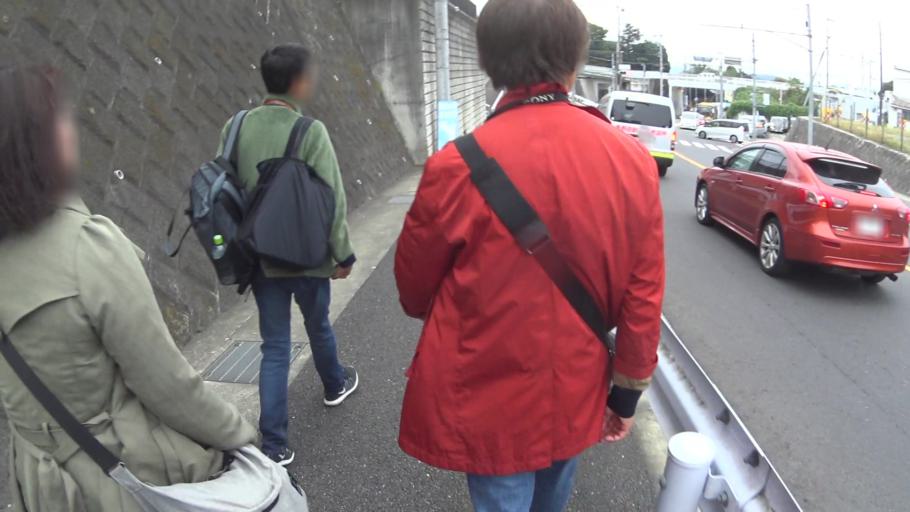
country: JP
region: Kanagawa
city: Hadano
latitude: 35.3807
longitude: 139.2185
